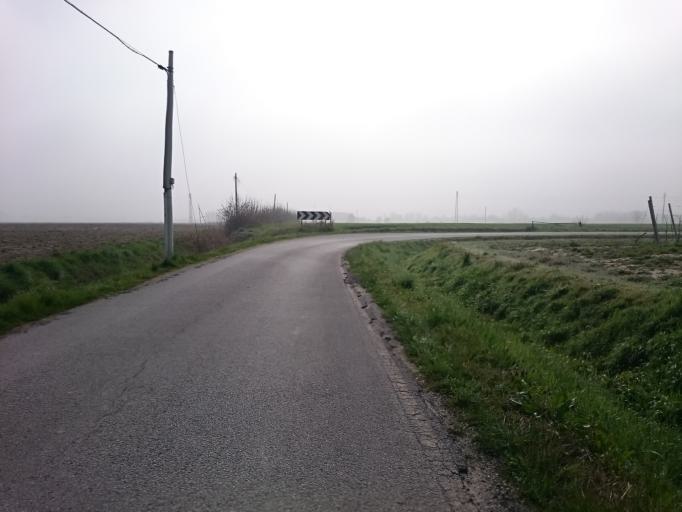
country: IT
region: Veneto
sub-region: Provincia di Padova
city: Due Carrare
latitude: 45.2910
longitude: 11.8376
